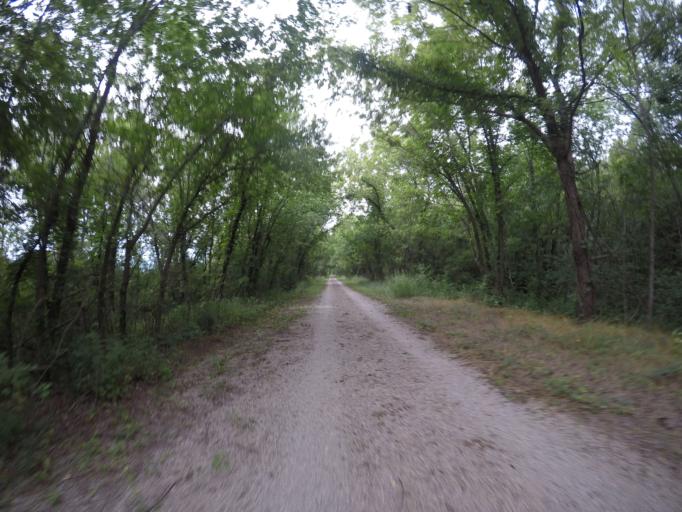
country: US
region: Kansas
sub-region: Franklin County
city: Ottawa
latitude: 38.5496
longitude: -95.2716
